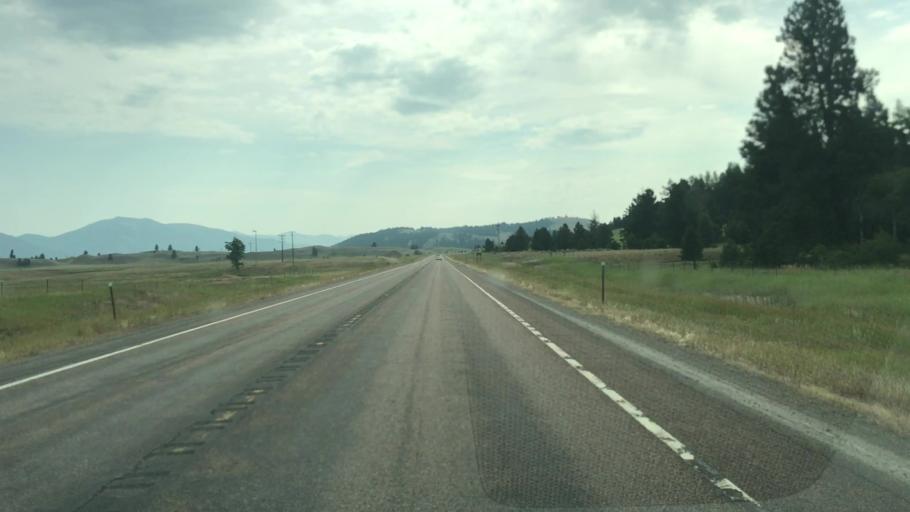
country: US
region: Montana
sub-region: Missoula County
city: Seeley Lake
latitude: 47.0304
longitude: -113.2685
